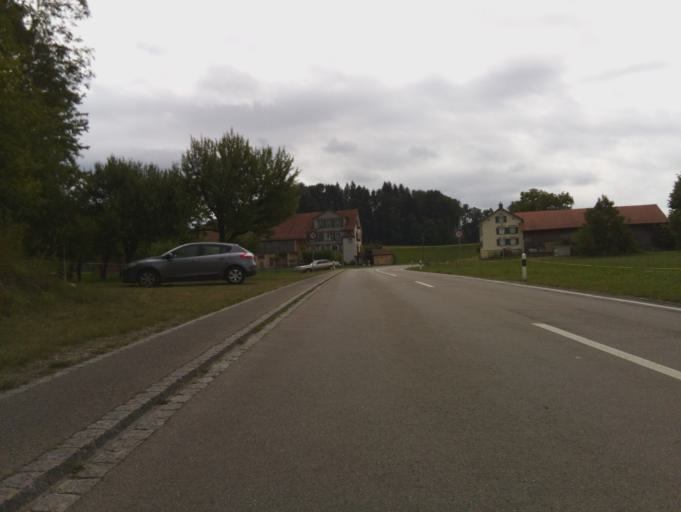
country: CH
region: Saint Gallen
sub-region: Wahlkreis Toggenburg
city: Lutisburg
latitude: 47.3920
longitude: 9.0857
